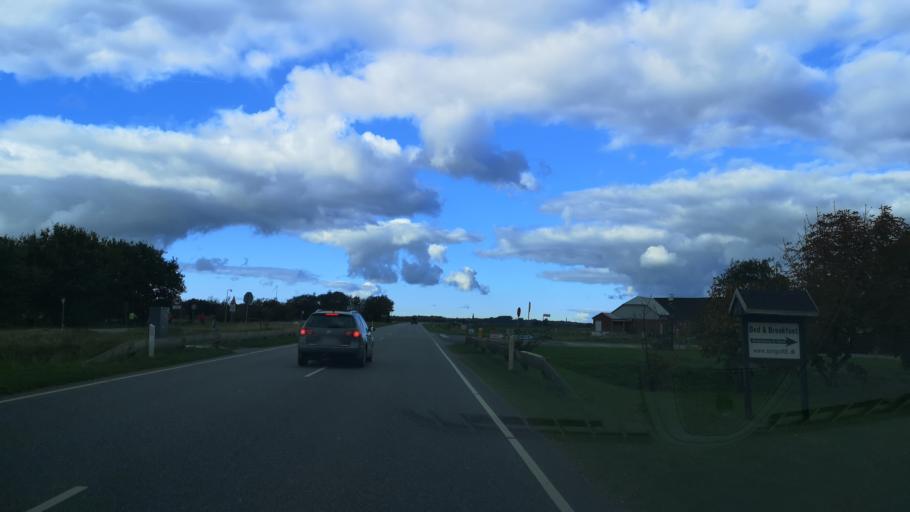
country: DK
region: South Denmark
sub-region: Tonder Kommune
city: Tonder
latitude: 54.9144
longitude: 8.9011
